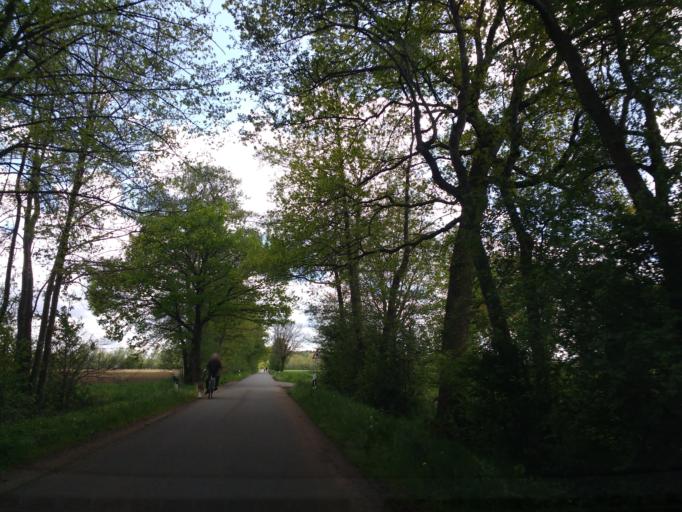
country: DE
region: North Rhine-Westphalia
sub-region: Regierungsbezirk Detmold
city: Hovelhof
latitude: 51.7793
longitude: 8.6580
